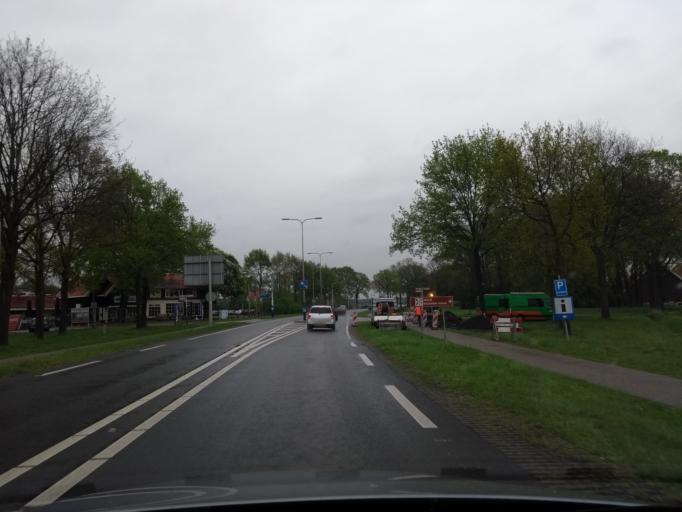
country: NL
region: Overijssel
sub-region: Gemeente Tubbergen
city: Tubbergen
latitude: 52.3799
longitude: 6.8055
